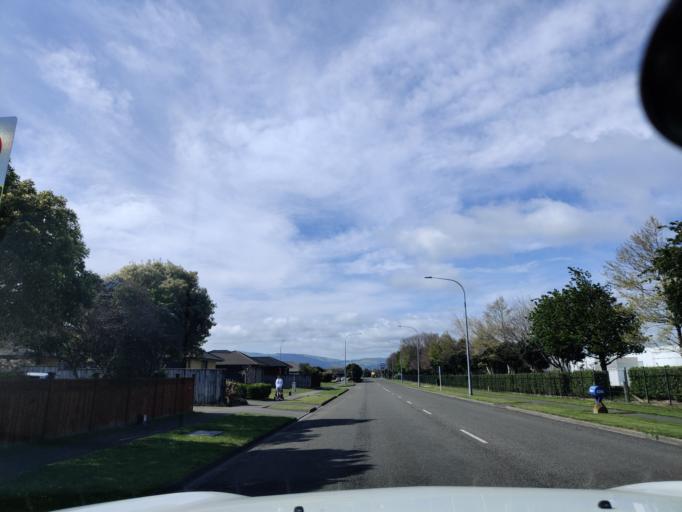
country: NZ
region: Manawatu-Wanganui
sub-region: Palmerston North City
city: Palmerston North
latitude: -40.3309
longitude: 175.6526
